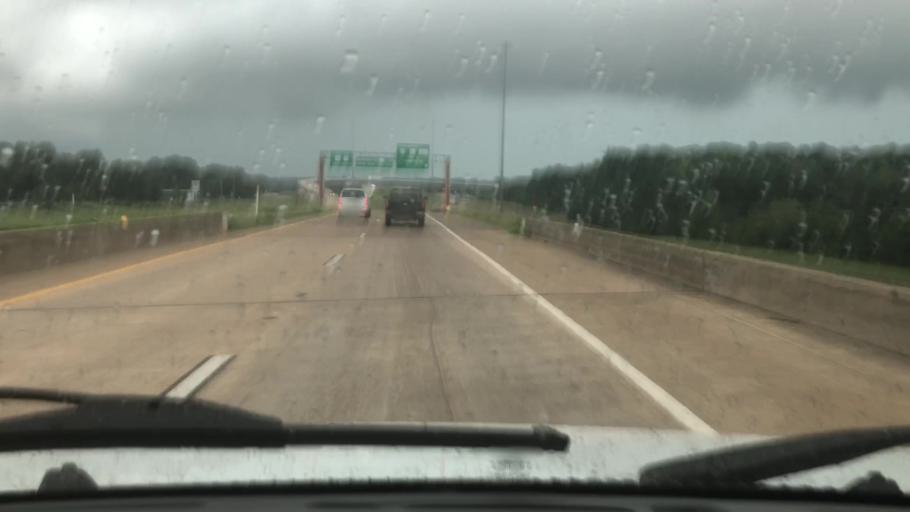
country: US
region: Texas
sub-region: Bowie County
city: Wake Village
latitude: 33.4021
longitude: -94.0979
